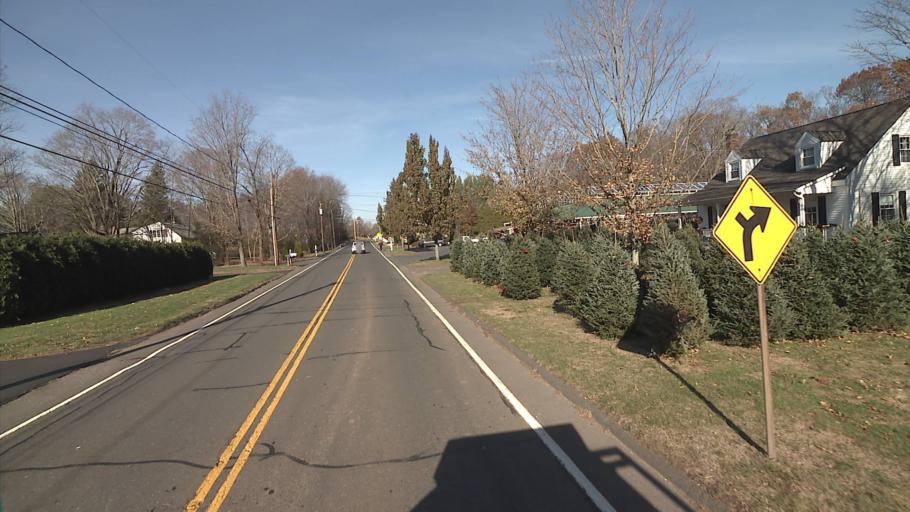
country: US
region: Connecticut
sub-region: Middlesex County
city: Cromwell
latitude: 41.6380
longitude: -72.6054
